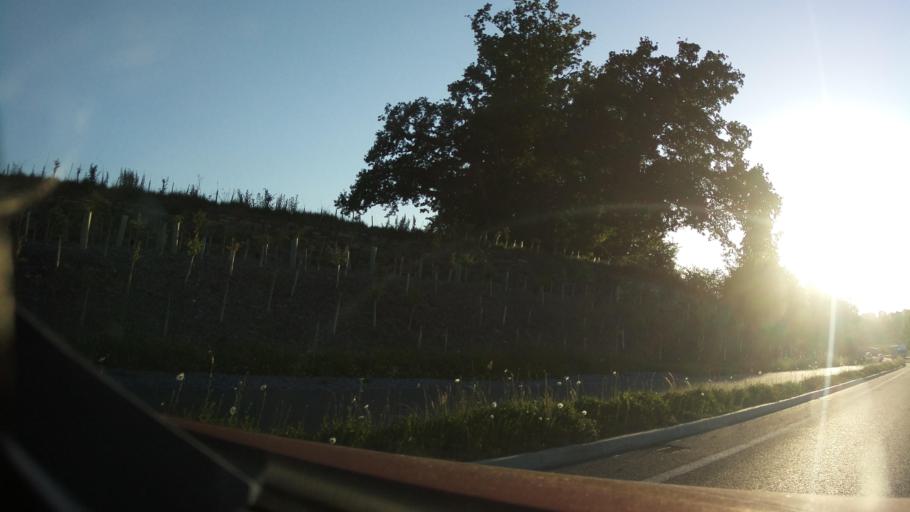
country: GB
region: England
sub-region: Devon
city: Newton Abbot
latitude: 50.5428
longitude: -3.6210
